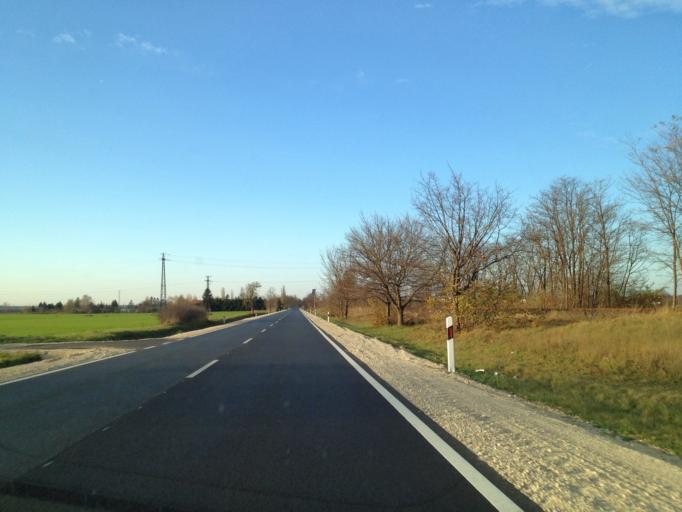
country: HU
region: Gyor-Moson-Sopron
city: Gyorujbarat
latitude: 47.6380
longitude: 17.6675
